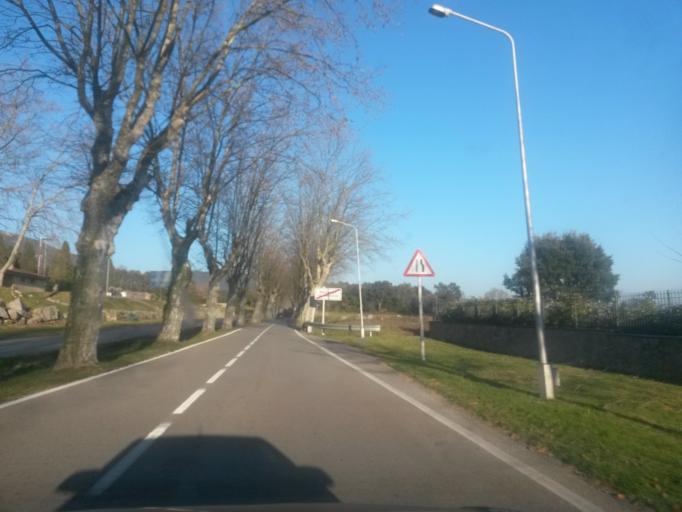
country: ES
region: Catalonia
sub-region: Provincia de Girona
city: Macanet de Cabrenys
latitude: 42.3863
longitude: 2.7555
